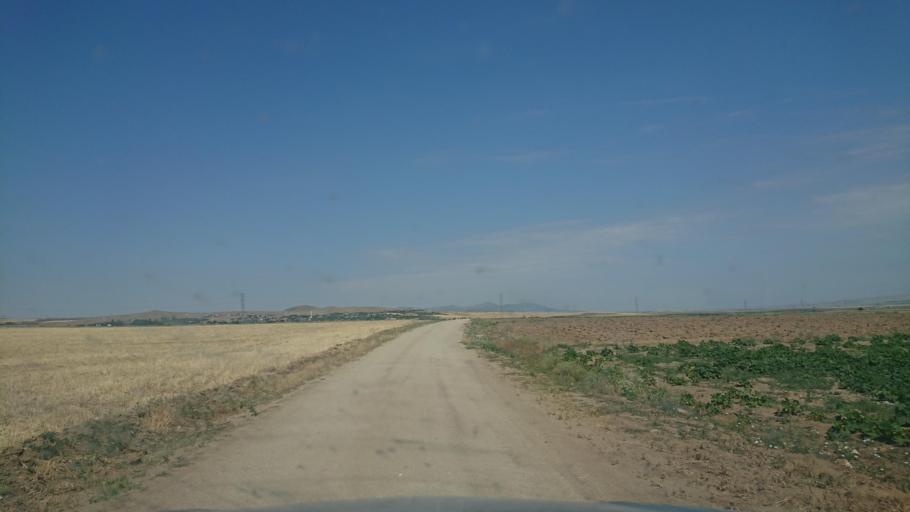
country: TR
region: Aksaray
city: Sariyahsi
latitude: 38.9572
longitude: 33.9121
